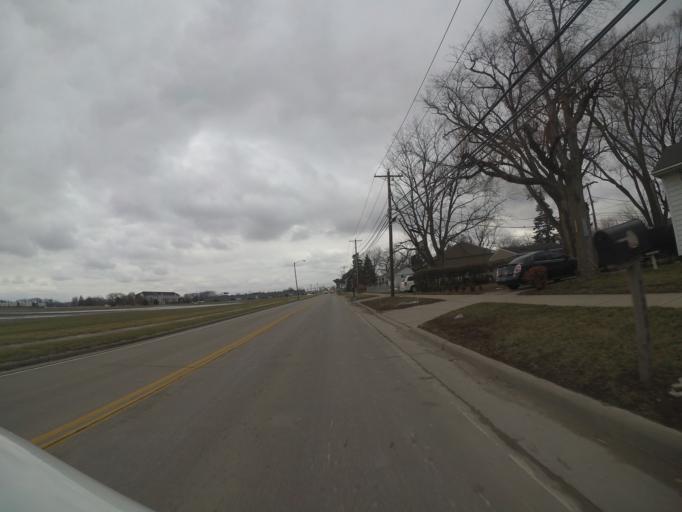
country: US
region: Ohio
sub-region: Wood County
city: Rossford
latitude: 41.6090
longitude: -83.5340
